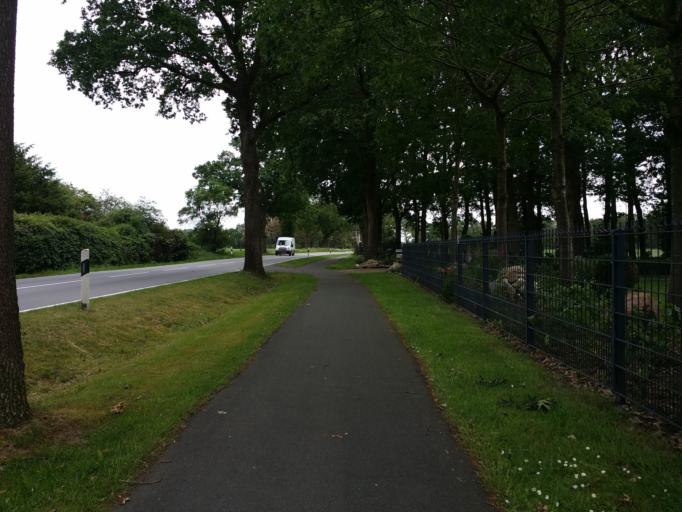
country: DE
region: Lower Saxony
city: Wiefelstede
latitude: 53.2775
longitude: 8.1094
